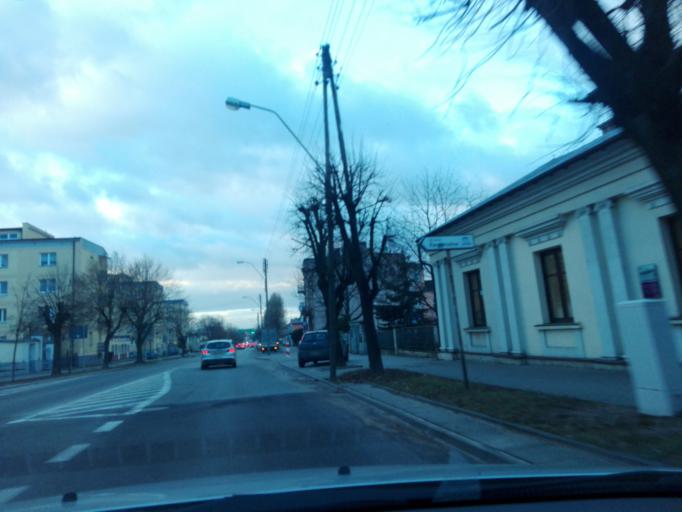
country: PL
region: Lodz Voivodeship
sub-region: Powiat kutnowski
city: Kutno
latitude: 52.2336
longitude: 19.3572
